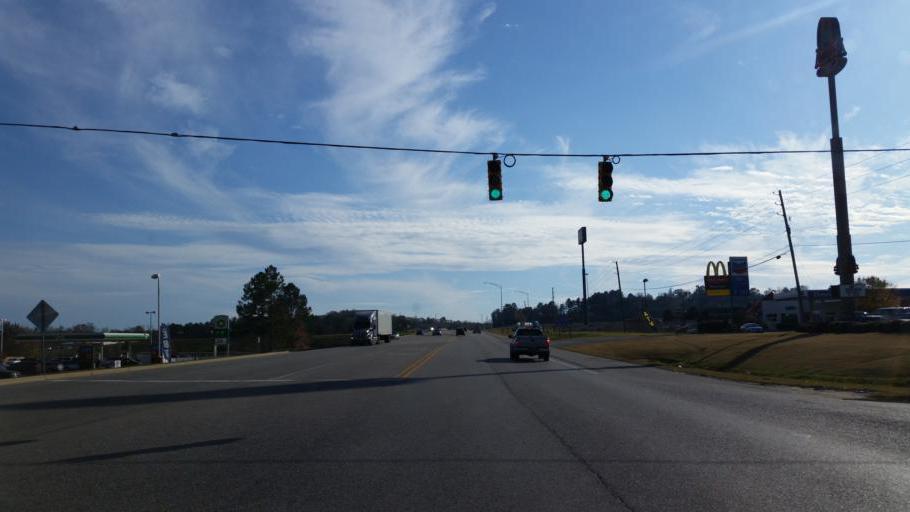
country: US
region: Alabama
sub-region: Tuscaloosa County
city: Holt
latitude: 33.1769
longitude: -87.4475
